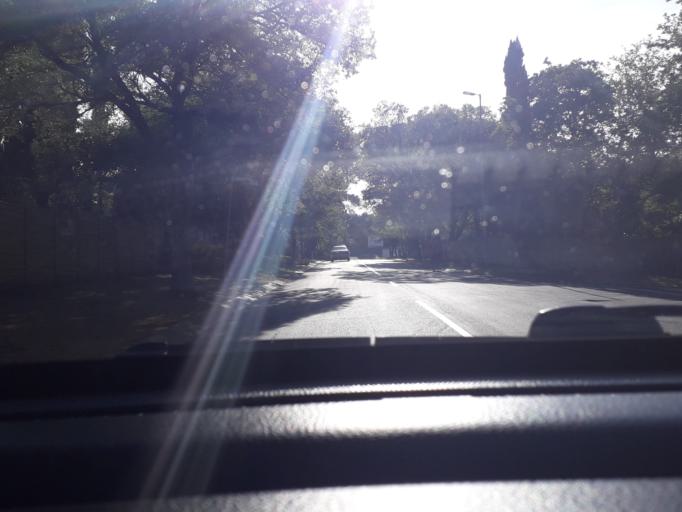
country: ZA
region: Gauteng
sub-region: City of Johannesburg Metropolitan Municipality
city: Modderfontein
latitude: -26.0771
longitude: 28.0805
